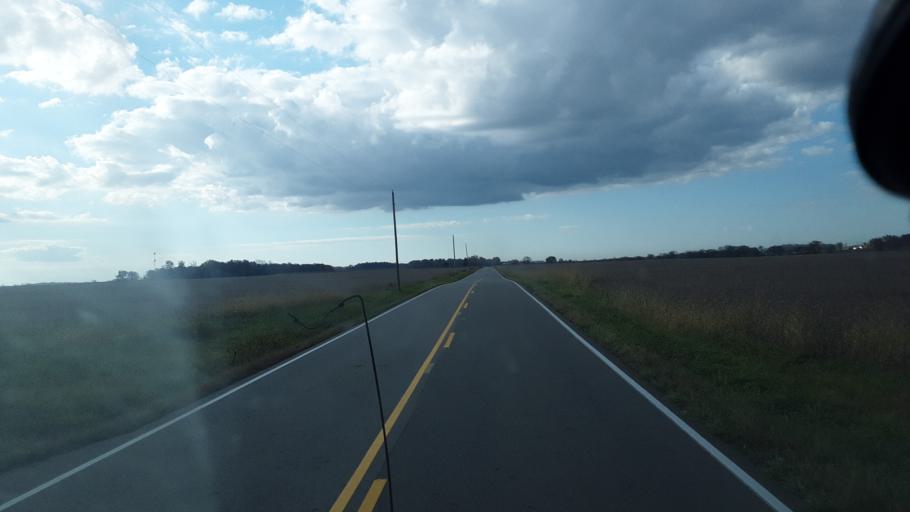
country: US
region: Ohio
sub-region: Highland County
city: Greenfield
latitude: 39.4352
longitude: -83.4399
